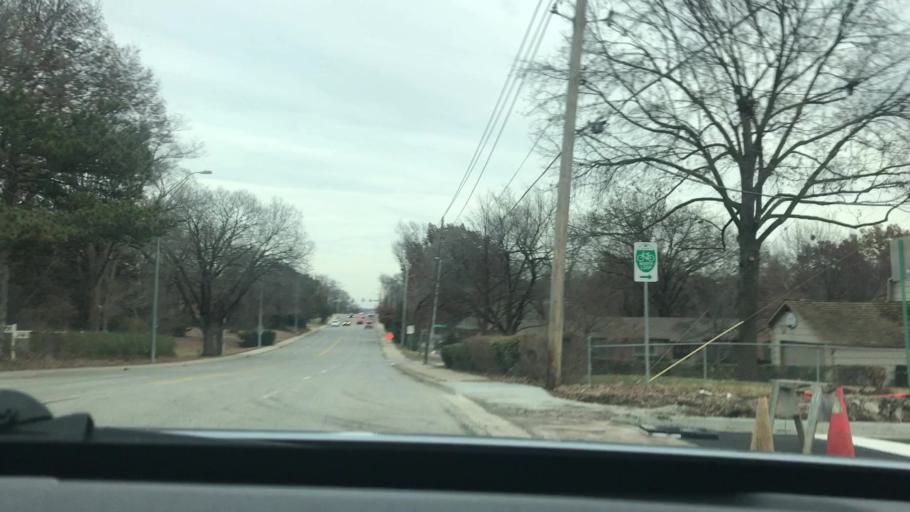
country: US
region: Kansas
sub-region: Johnson County
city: Leawood
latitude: 38.9421
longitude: -94.6239
